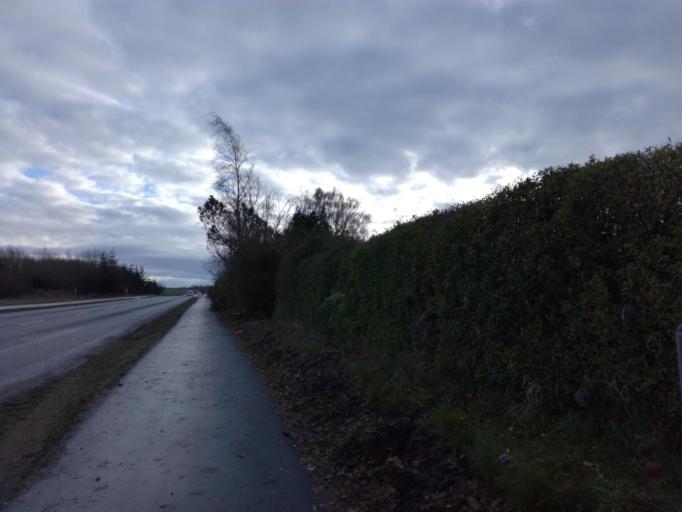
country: DK
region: South Denmark
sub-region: Fredericia Kommune
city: Fredericia
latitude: 55.6110
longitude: 9.7503
